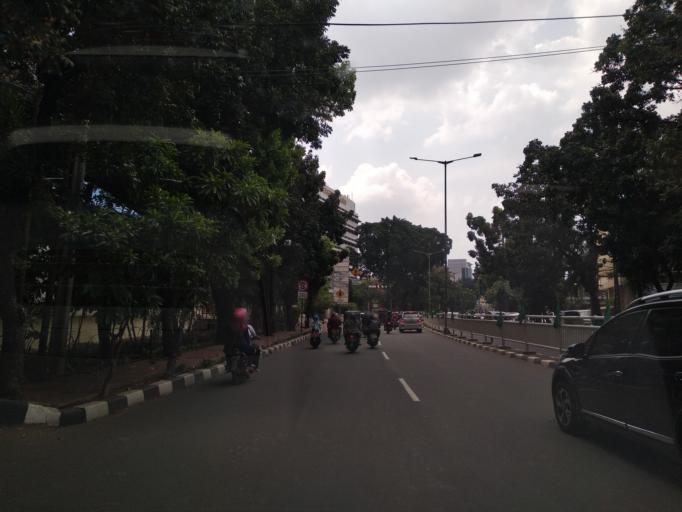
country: ID
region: Jakarta Raya
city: Jakarta
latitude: -6.2375
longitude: 106.8446
